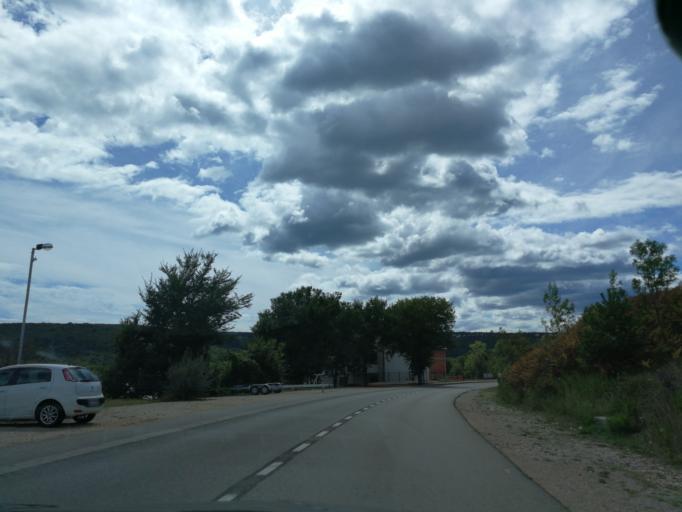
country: HR
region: Primorsko-Goranska
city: Njivice
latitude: 45.1546
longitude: 14.5976
